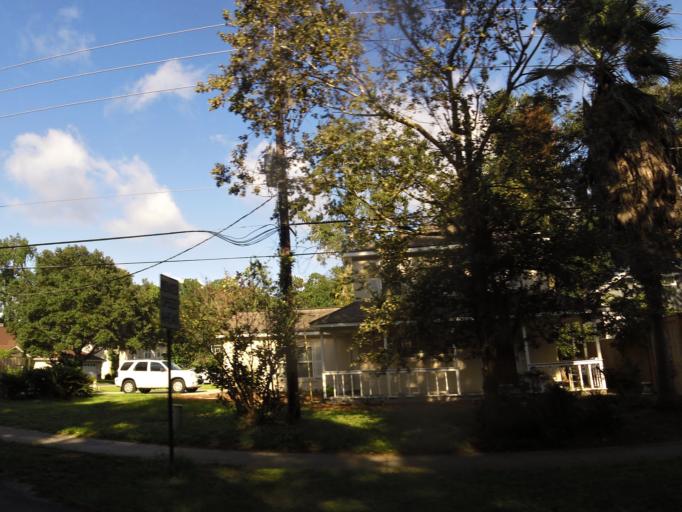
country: US
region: Georgia
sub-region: Glynn County
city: Saint Simon Mills
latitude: 31.2132
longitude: -81.3755
